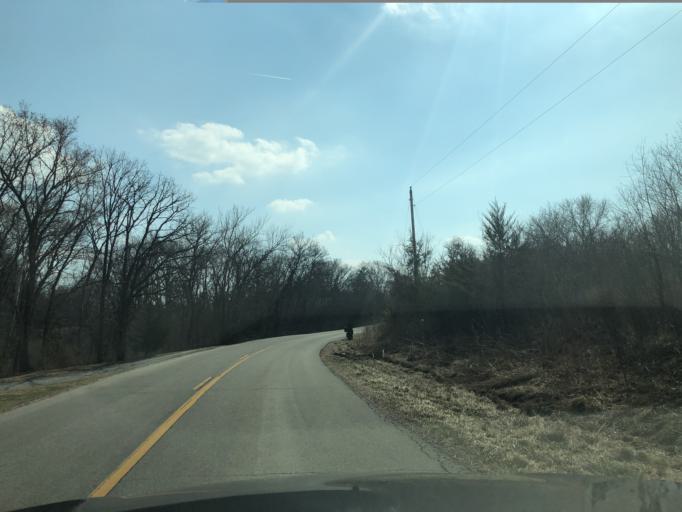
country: US
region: Missouri
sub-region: Platte County
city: Weston
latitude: 39.4495
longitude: -94.8517
